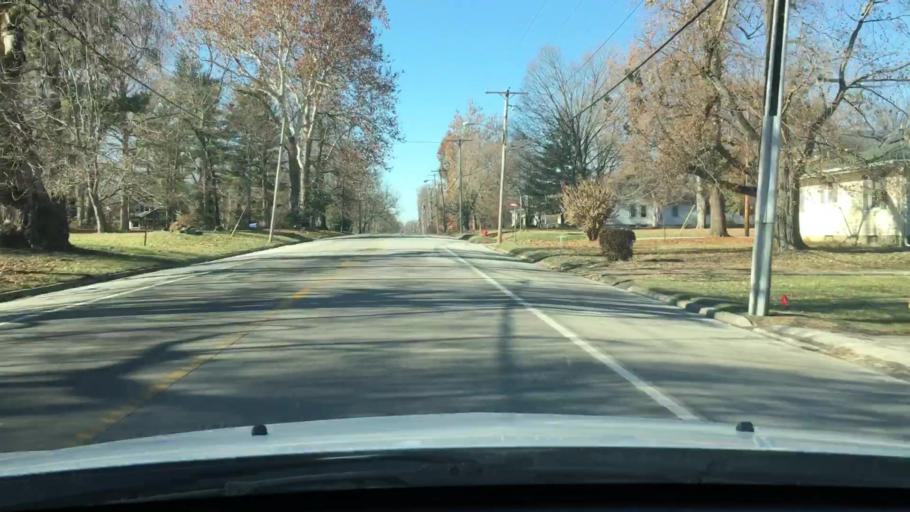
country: US
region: Illinois
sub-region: Pike County
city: Pittsfield
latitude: 39.6068
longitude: -90.7926
